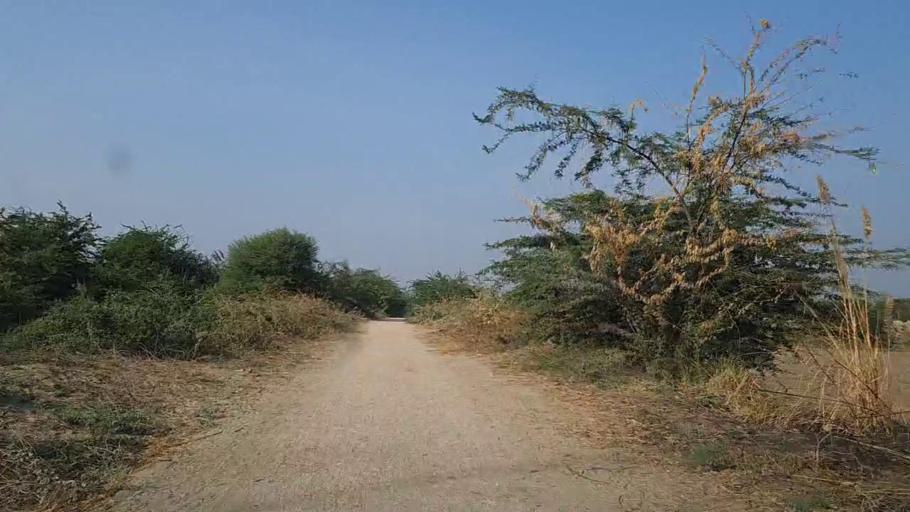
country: PK
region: Sindh
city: Mirpur Sakro
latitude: 24.5989
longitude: 67.6492
